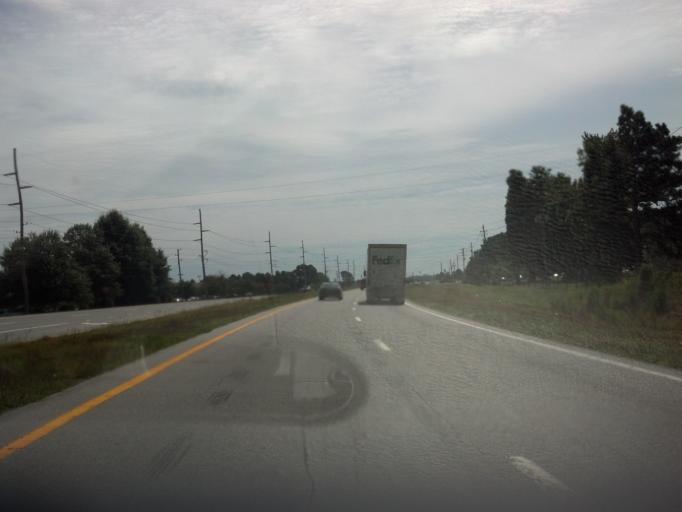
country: US
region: North Carolina
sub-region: Pitt County
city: Greenville
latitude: 35.6557
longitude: -77.3500
